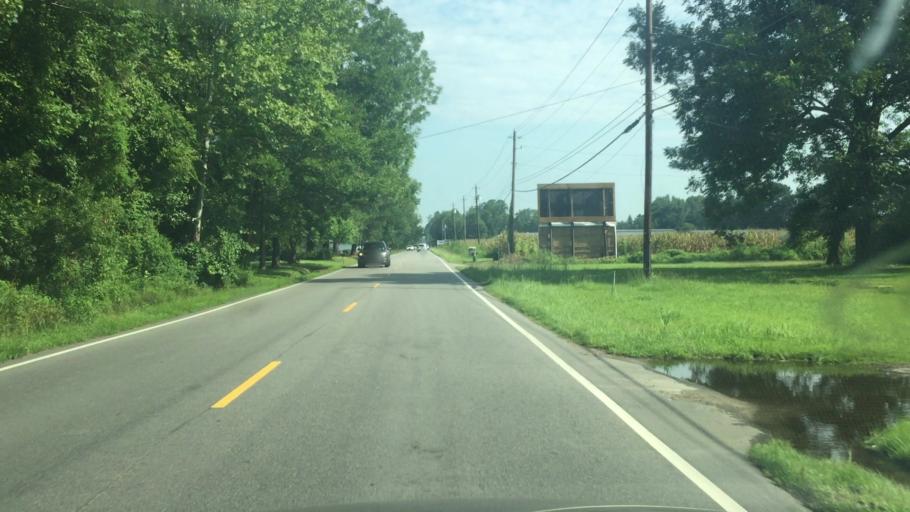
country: US
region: North Carolina
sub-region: Columbus County
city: Chadbourn
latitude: 34.3072
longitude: -78.8264
